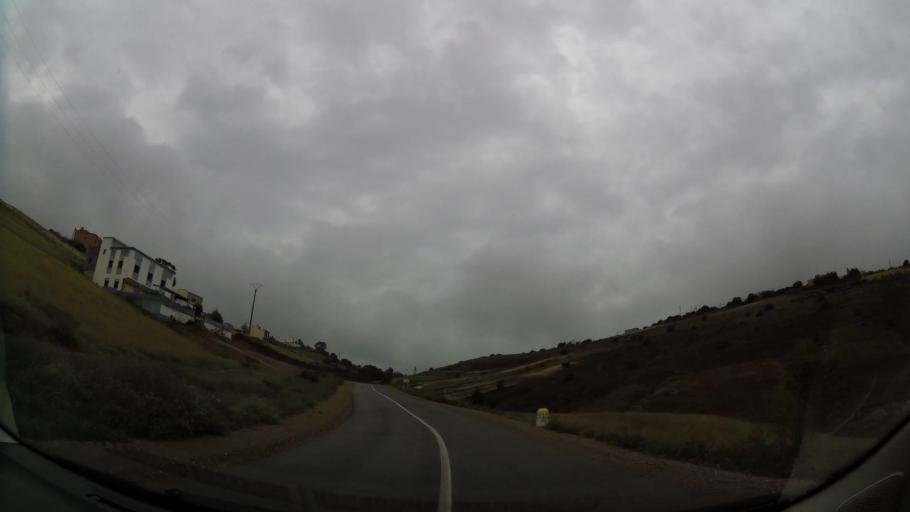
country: MA
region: Oriental
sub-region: Nador
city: Nador
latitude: 35.1343
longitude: -3.0547
